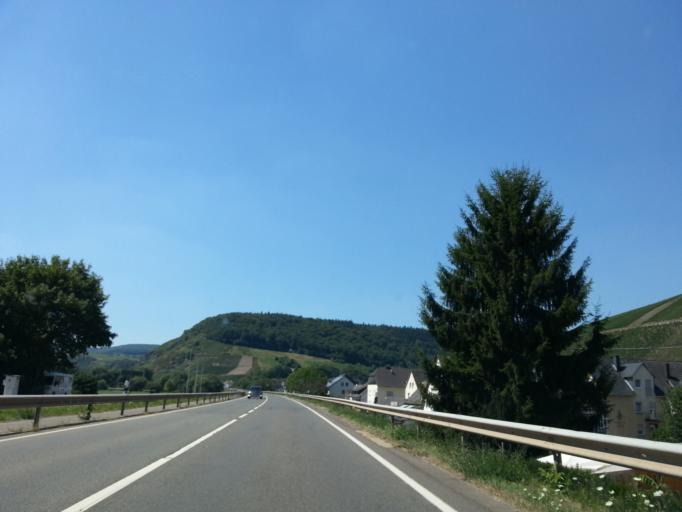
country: DE
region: Rheinland-Pfalz
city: Klusserath
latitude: 49.8435
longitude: 6.8562
